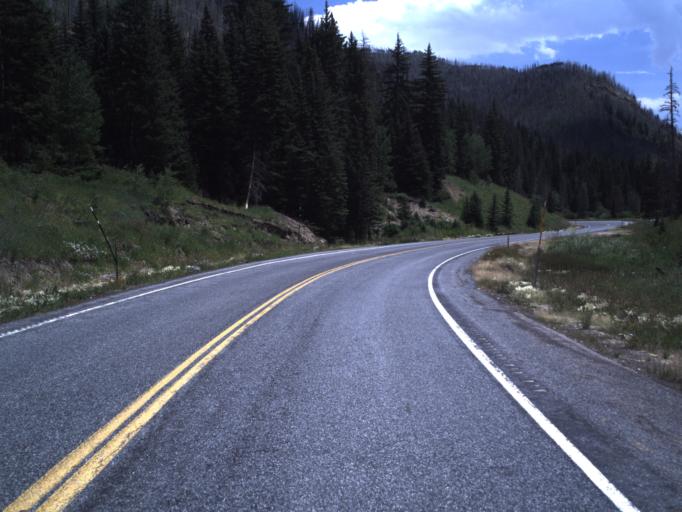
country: US
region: Utah
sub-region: Sanpete County
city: Fairview
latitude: 39.5697
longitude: -111.1813
